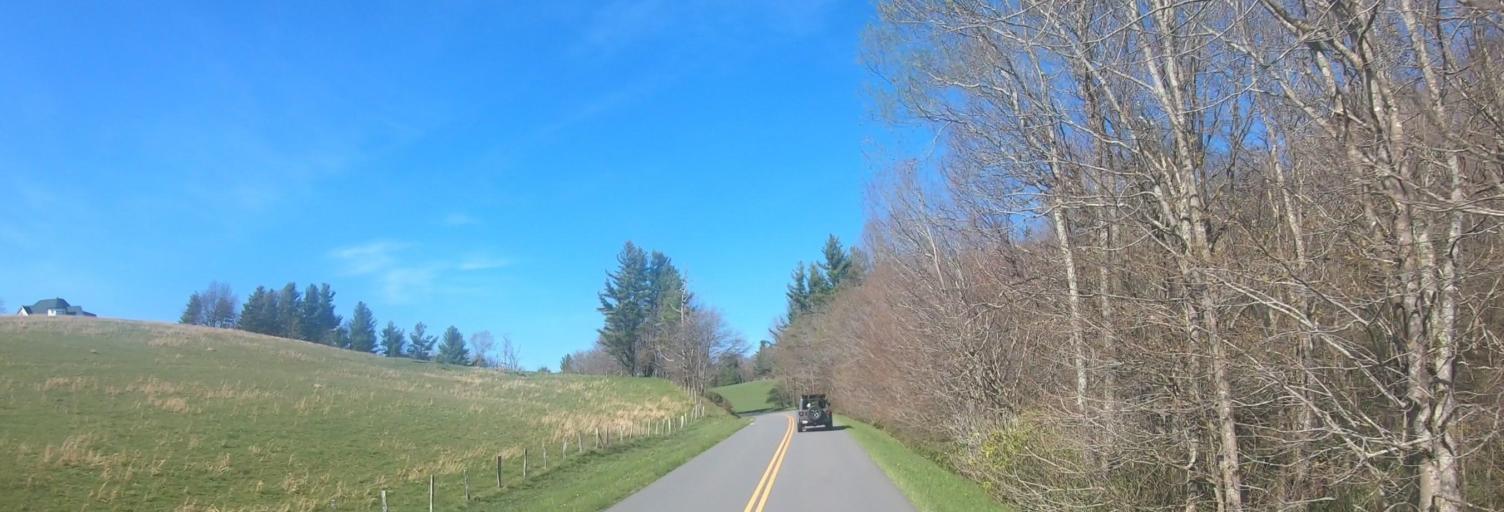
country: US
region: North Carolina
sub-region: Watauga County
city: Blowing Rock
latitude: 36.1521
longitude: -81.6231
